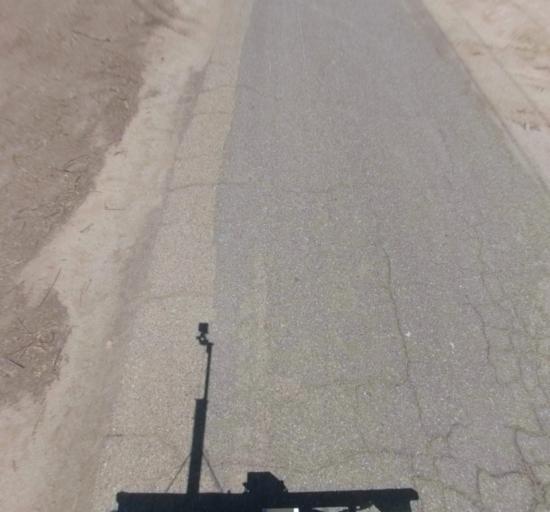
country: US
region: California
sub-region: Madera County
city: Chowchilla
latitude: 36.9993
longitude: -120.3285
